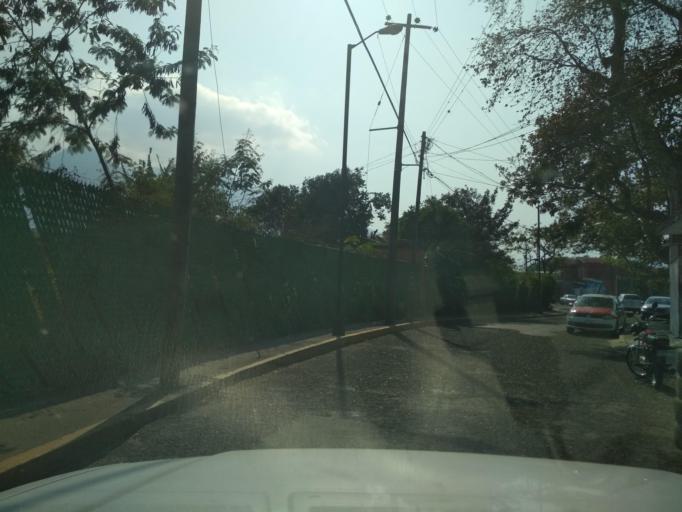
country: MX
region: Veracruz
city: Jalapilla
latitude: 18.8384
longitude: -97.0858
